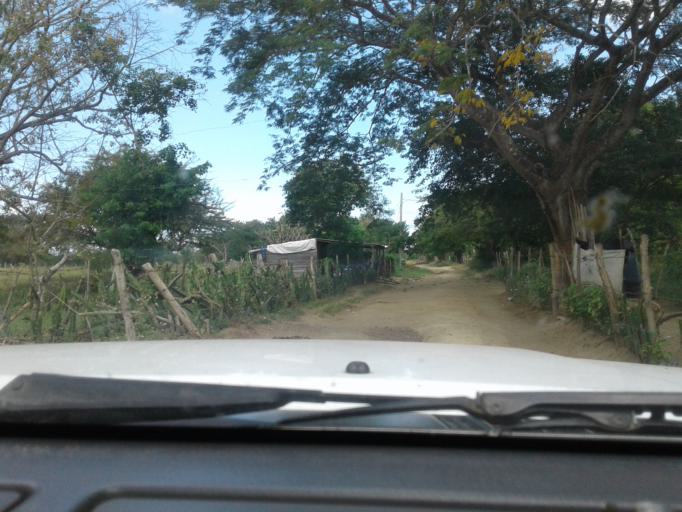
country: NI
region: Rivas
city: Belen
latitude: 11.6316
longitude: -85.9533
